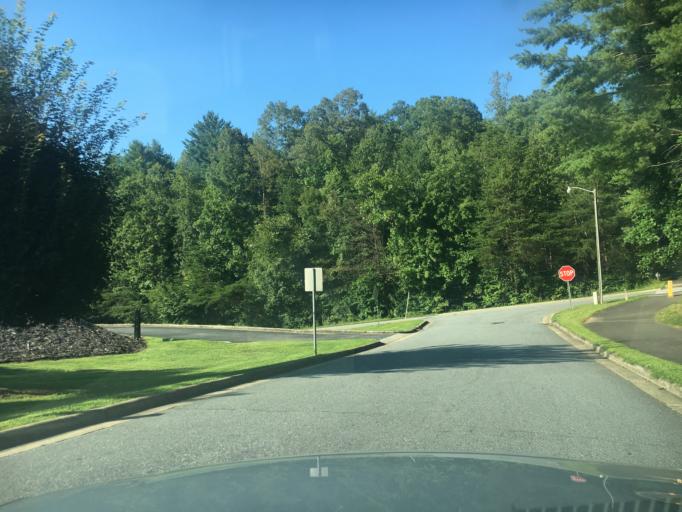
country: US
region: North Carolina
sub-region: McDowell County
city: West Marion
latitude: 35.6659
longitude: -82.0247
